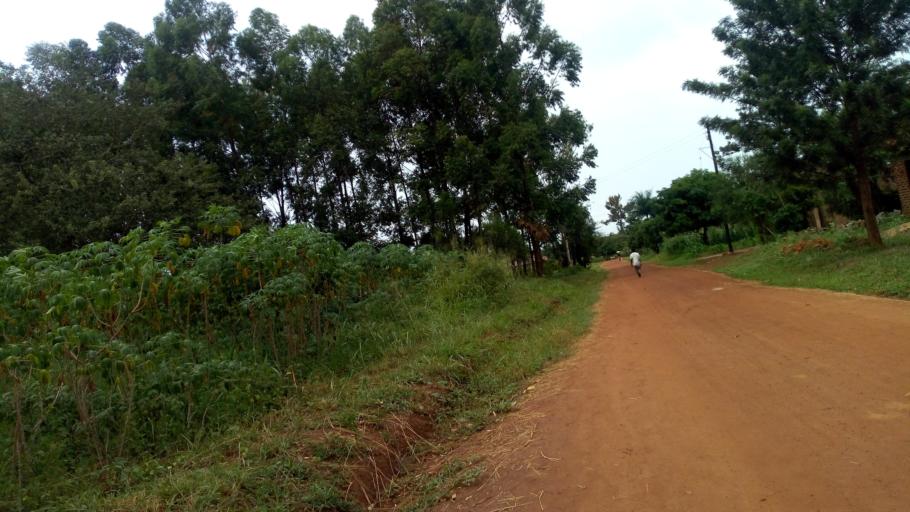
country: UG
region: Western Region
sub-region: Kiryandongo District
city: Kiryandongo
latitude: 1.7996
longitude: 32.0084
